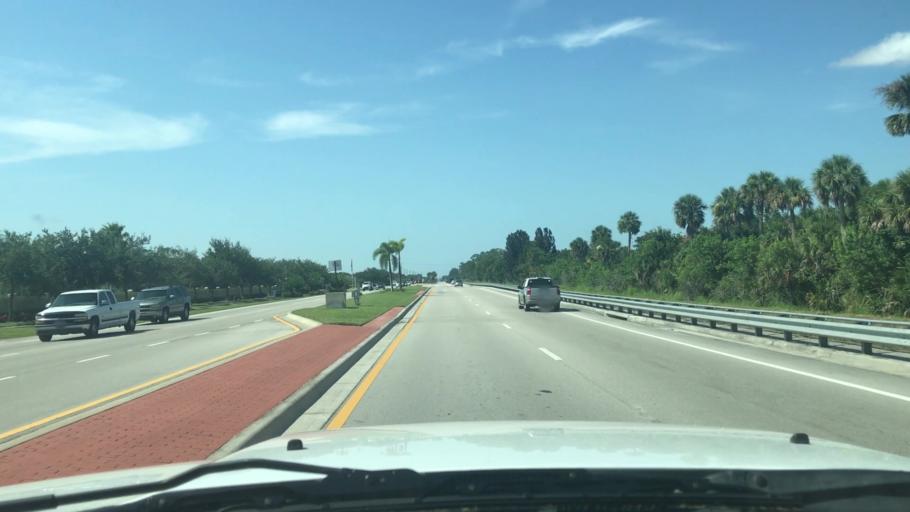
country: US
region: Florida
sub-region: Indian River County
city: West Vero Corridor
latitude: 27.6470
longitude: -80.4632
